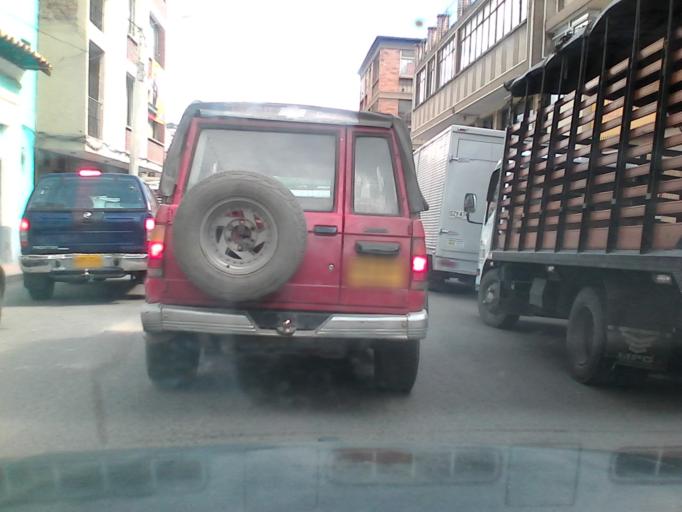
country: CO
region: Boyaca
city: Duitama
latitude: 5.8249
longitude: -73.0338
